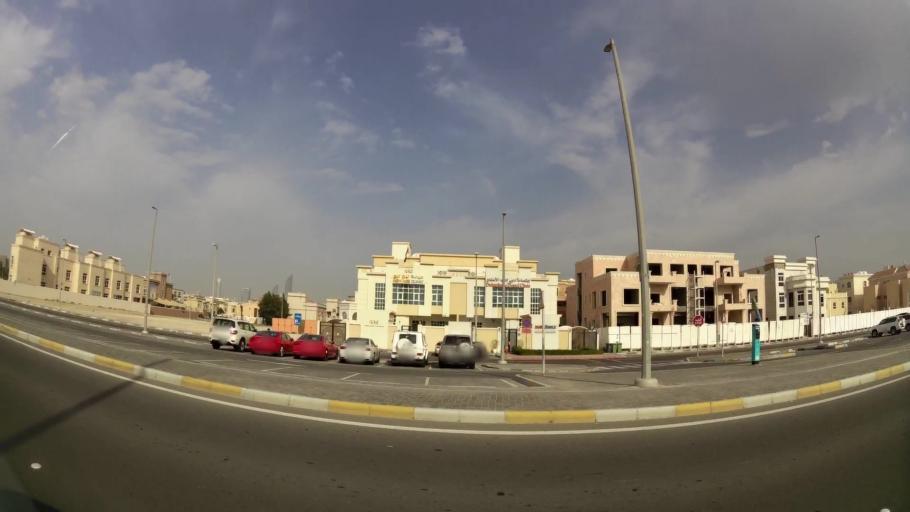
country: AE
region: Abu Dhabi
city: Abu Dhabi
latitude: 24.4716
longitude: 54.3885
